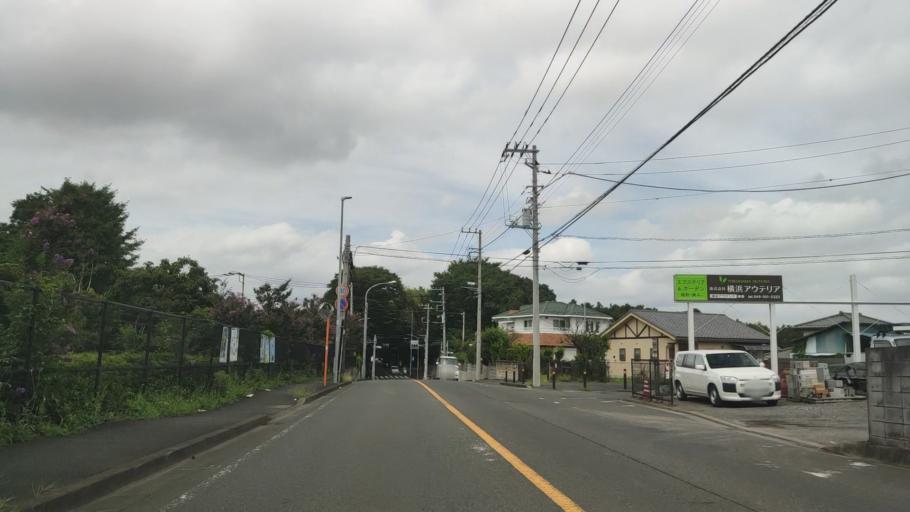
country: JP
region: Kanagawa
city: Minami-rinkan
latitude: 35.4826
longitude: 139.4750
